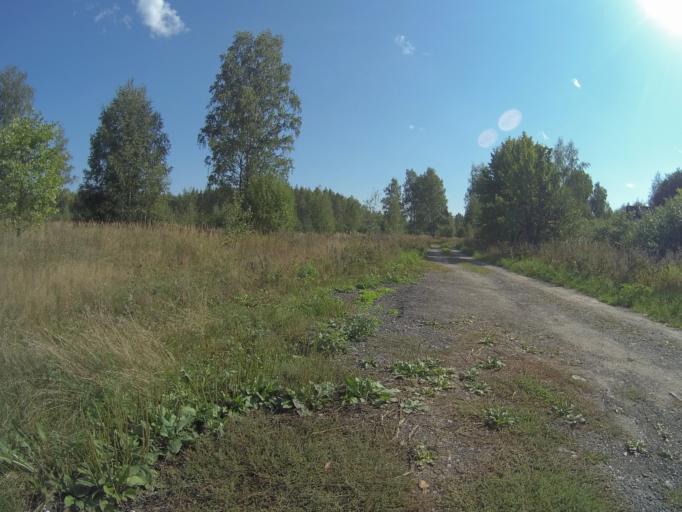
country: RU
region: Vladimir
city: Raduzhnyy
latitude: 55.9903
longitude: 40.2616
